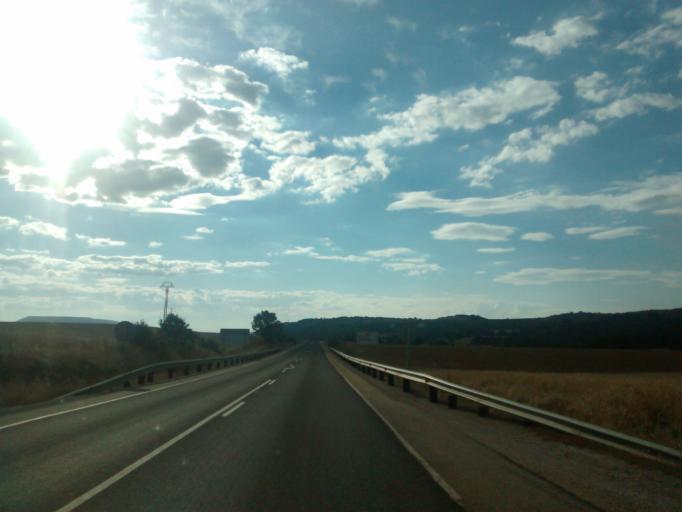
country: ES
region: Castille and Leon
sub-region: Provincia de Burgos
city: Basconcillos del Tozo
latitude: 42.6752
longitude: -3.9381
